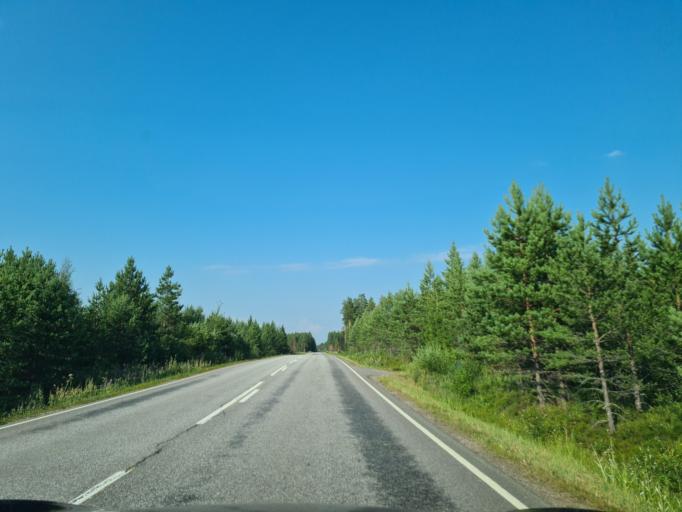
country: FI
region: Satakunta
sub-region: Pohjois-Satakunta
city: Karvia
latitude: 62.2953
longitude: 22.6236
